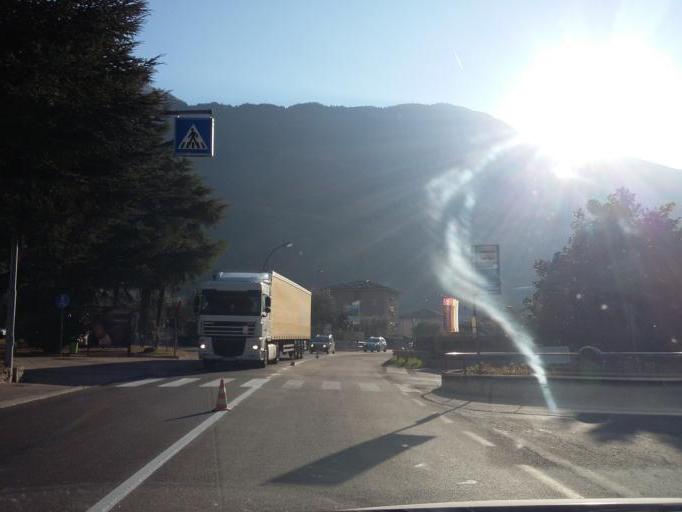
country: IT
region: Trentino-Alto Adige
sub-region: Provincia di Trento
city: Bolognano-Vignole
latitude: 45.9110
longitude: 10.9003
